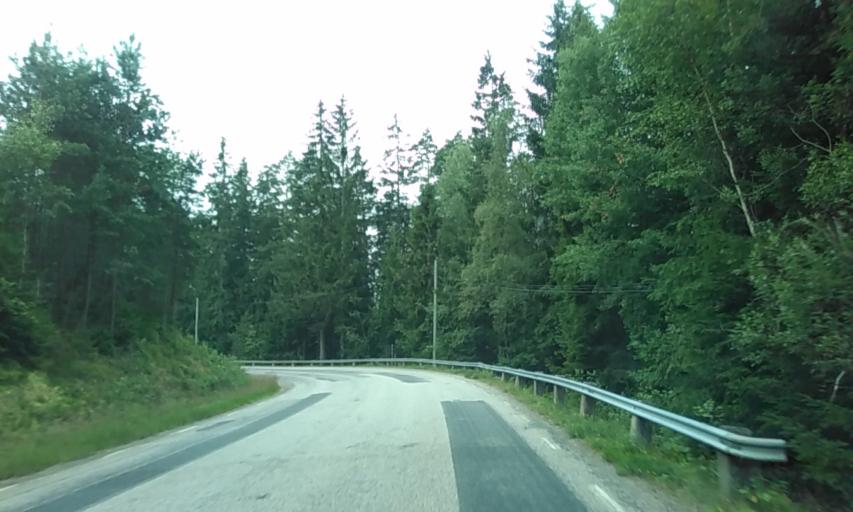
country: SE
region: Vaestra Goetaland
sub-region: Bollebygds Kommun
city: Bollebygd
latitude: 57.7821
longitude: 12.6279
